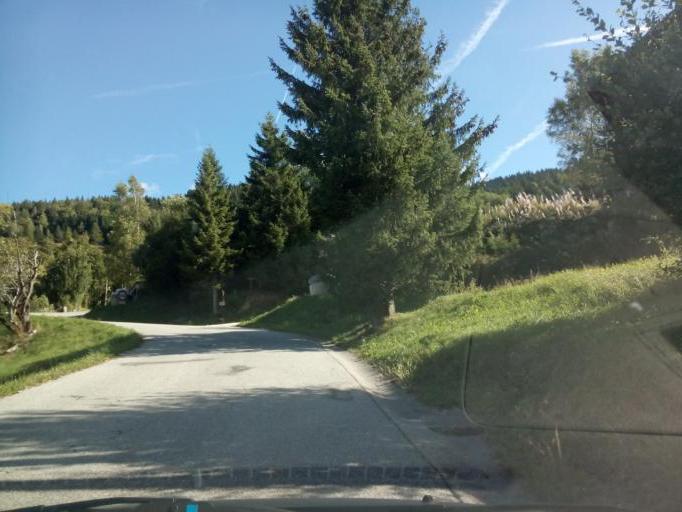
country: FR
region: Rhone-Alpes
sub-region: Departement de l'Isere
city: Vaulnaveys-le-Bas
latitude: 45.0383
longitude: 5.8504
